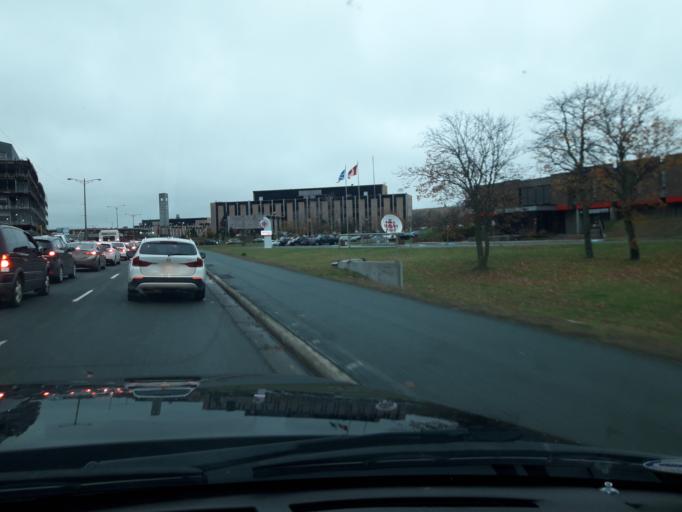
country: CA
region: Newfoundland and Labrador
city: St. John's
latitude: 47.5702
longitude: -52.7395
